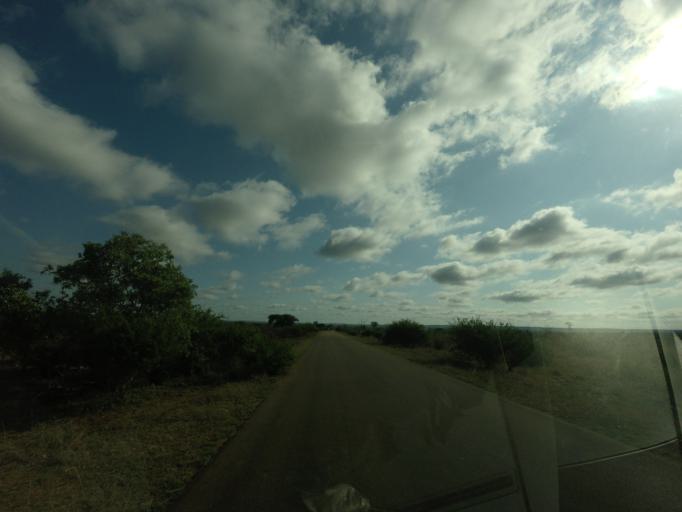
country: ZA
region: Mpumalanga
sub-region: Ehlanzeni District
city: Komatipoort
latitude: -25.1710
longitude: 31.9180
